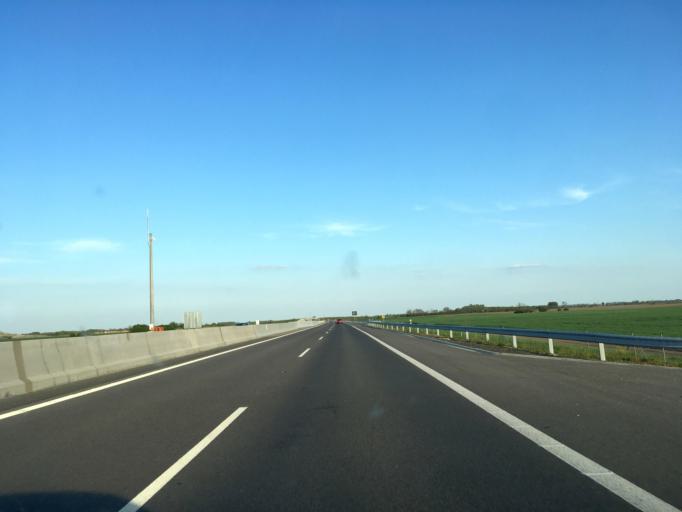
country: SK
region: Trnavsky
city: Samorin
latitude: 48.0348
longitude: 17.3558
